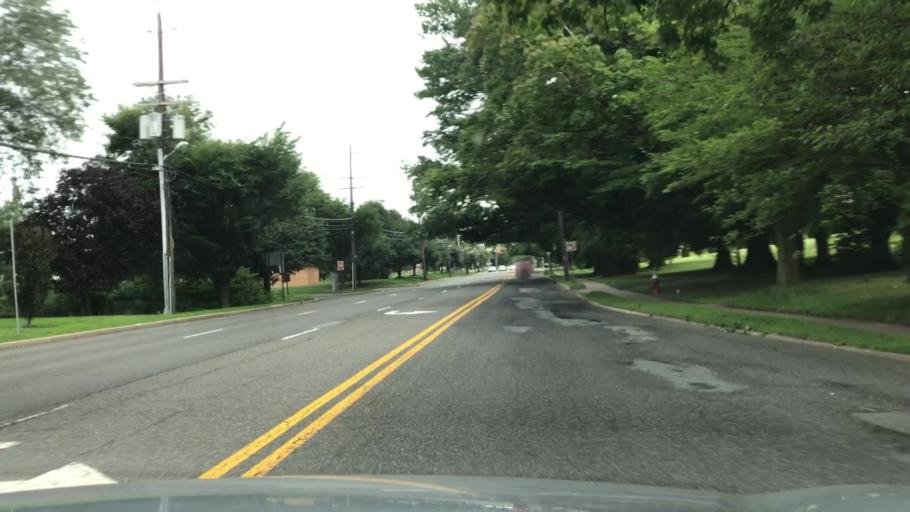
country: US
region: New Jersey
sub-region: Bergen County
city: Oradell
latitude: 40.9625
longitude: -74.0307
